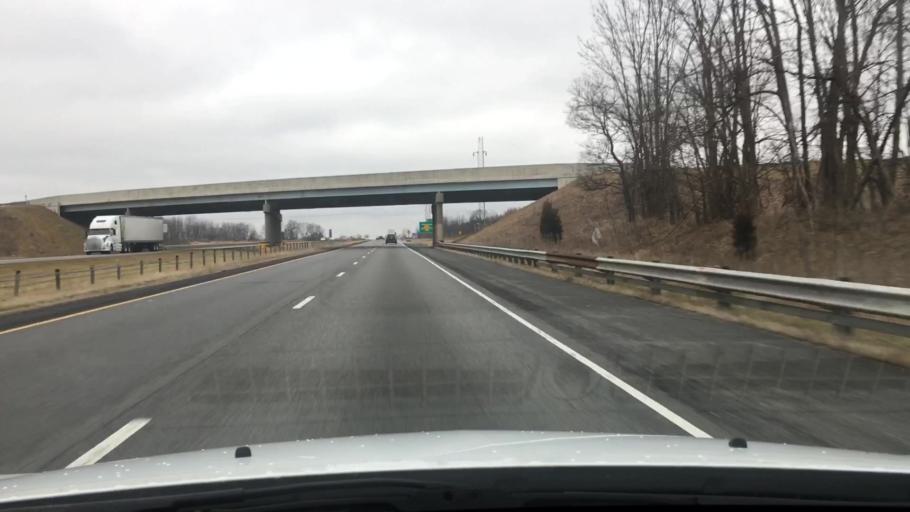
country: US
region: Indiana
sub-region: Boone County
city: Whitestown
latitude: 39.9304
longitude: -86.3385
